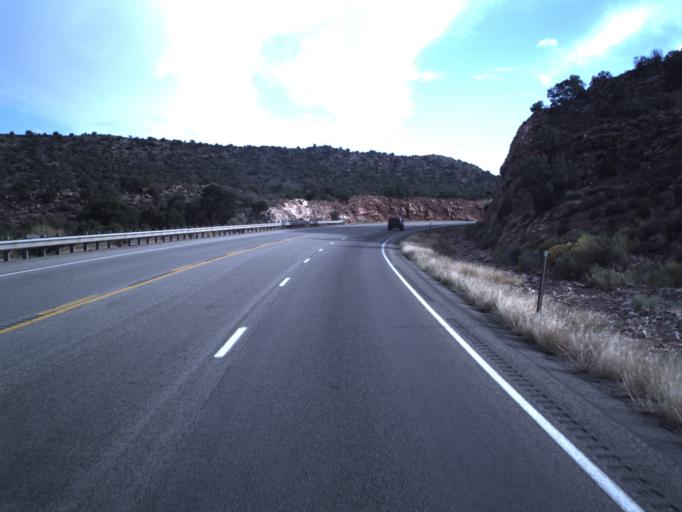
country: US
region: Utah
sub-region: Grand County
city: Moab
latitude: 38.4278
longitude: -109.4276
